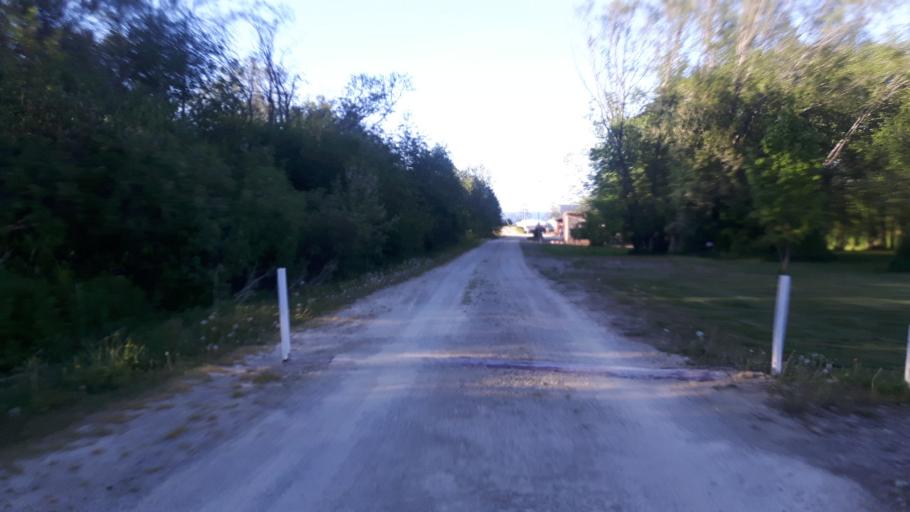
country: EE
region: Ida-Virumaa
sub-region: Kivioli linn
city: Kivioli
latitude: 59.4332
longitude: 26.9531
